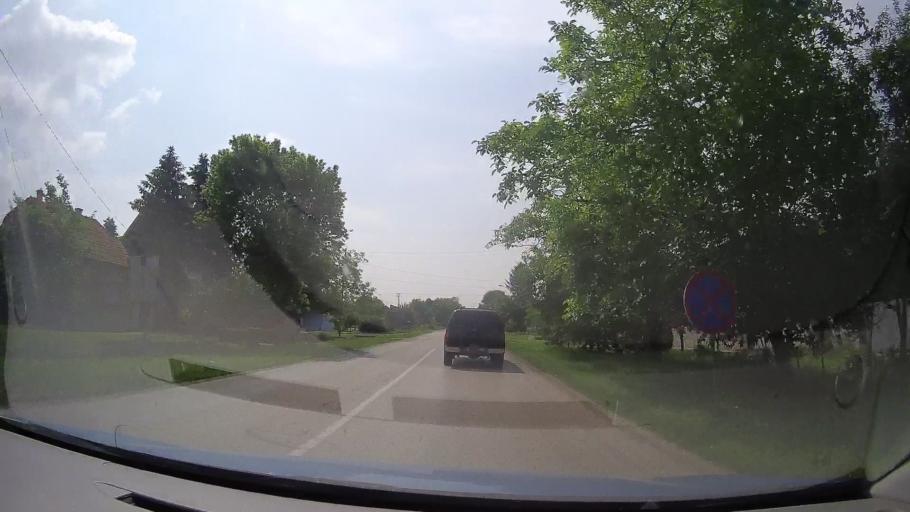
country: RS
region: Autonomna Pokrajina Vojvodina
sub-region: Juznobanatski Okrug
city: Kovacica
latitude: 45.1038
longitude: 20.6224
